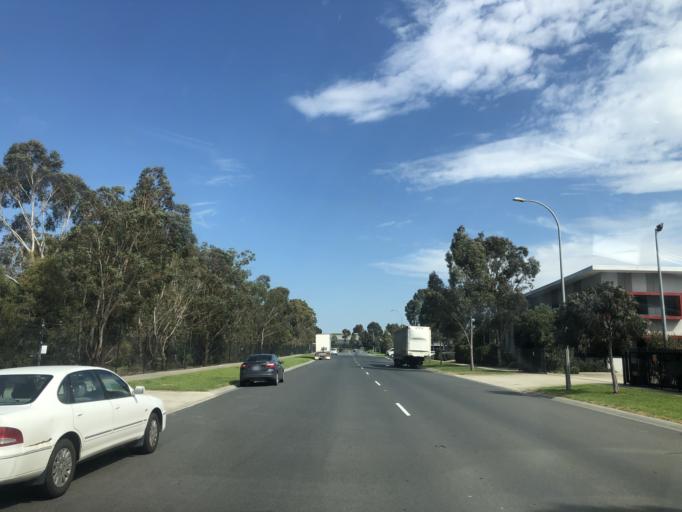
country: AU
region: Victoria
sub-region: Casey
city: Hampton Park
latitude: -38.0380
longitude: 145.2340
